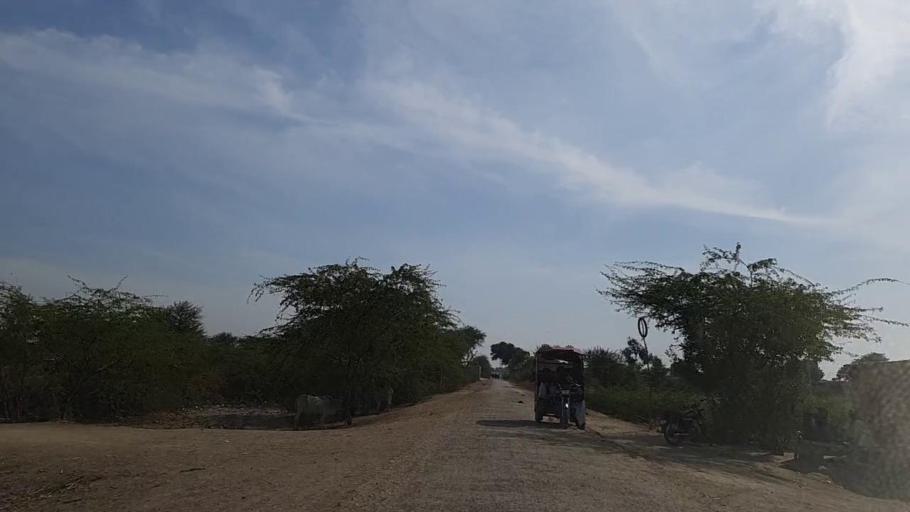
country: PK
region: Sindh
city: Samaro
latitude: 25.2235
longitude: 69.4323
